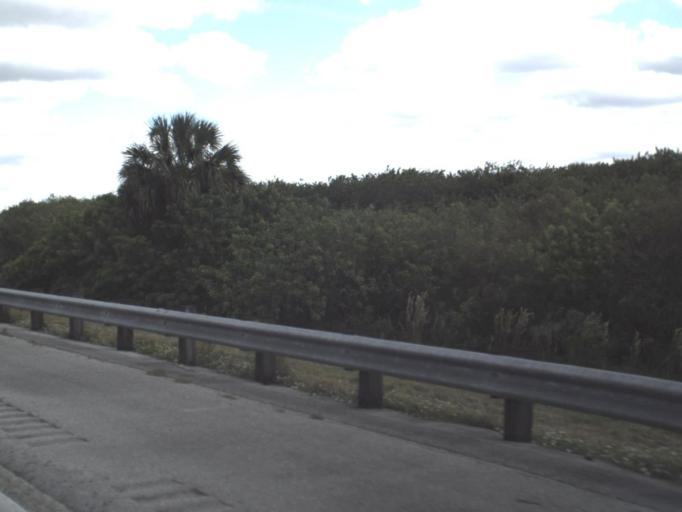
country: US
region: Florida
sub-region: Indian River County
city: Fellsmere
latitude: 27.5593
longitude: -80.7159
